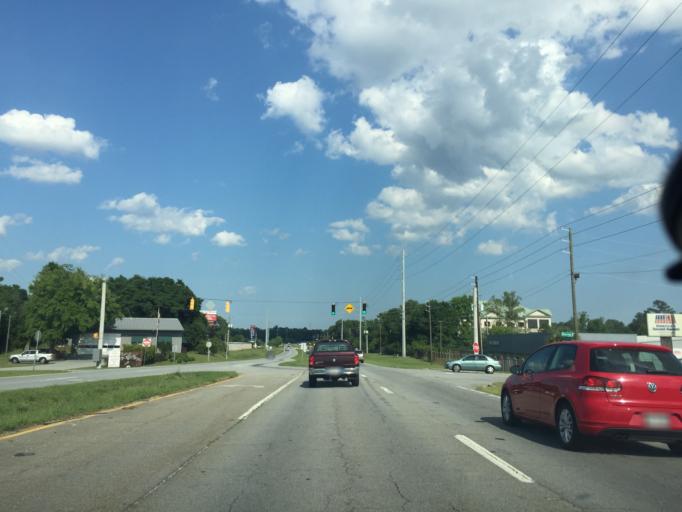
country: US
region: Georgia
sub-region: Chatham County
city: Thunderbolt
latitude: 32.0666
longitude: -81.0449
